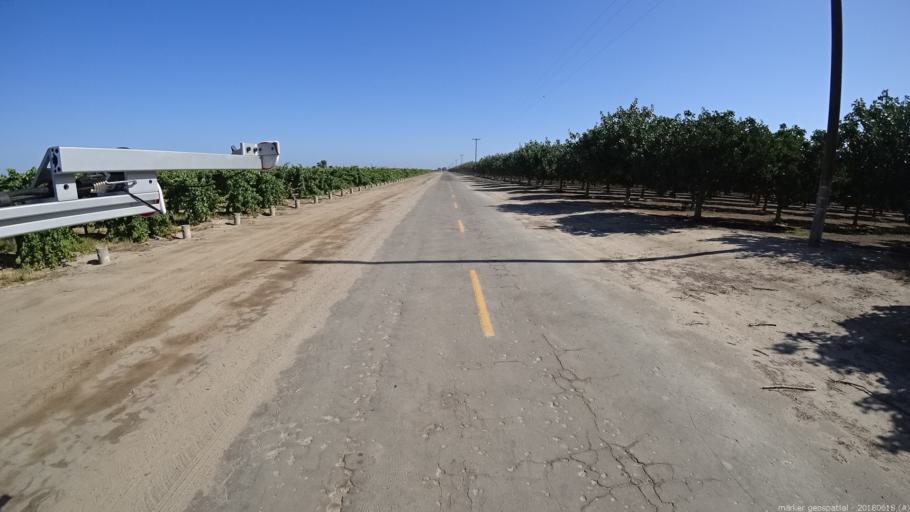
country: US
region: California
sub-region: Madera County
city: Parkwood
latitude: 36.8884
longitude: -120.1558
